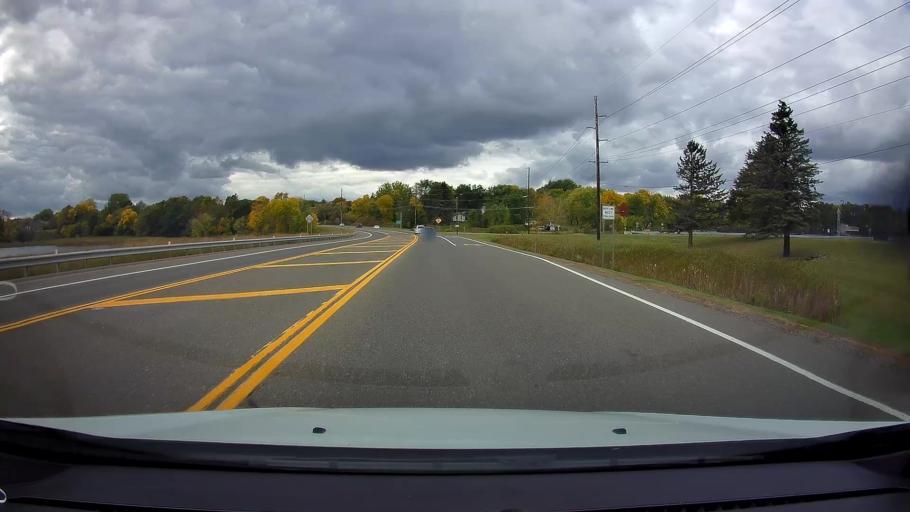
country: US
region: Minnesota
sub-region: Chisago County
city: Center City
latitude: 45.3903
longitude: -92.8295
